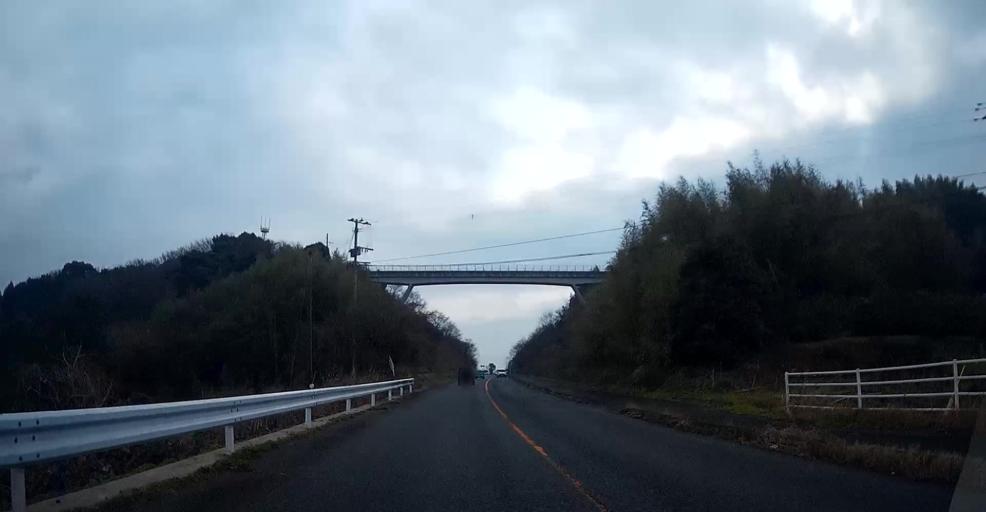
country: JP
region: Kumamoto
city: Matsubase
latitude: 32.6268
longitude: 130.5335
